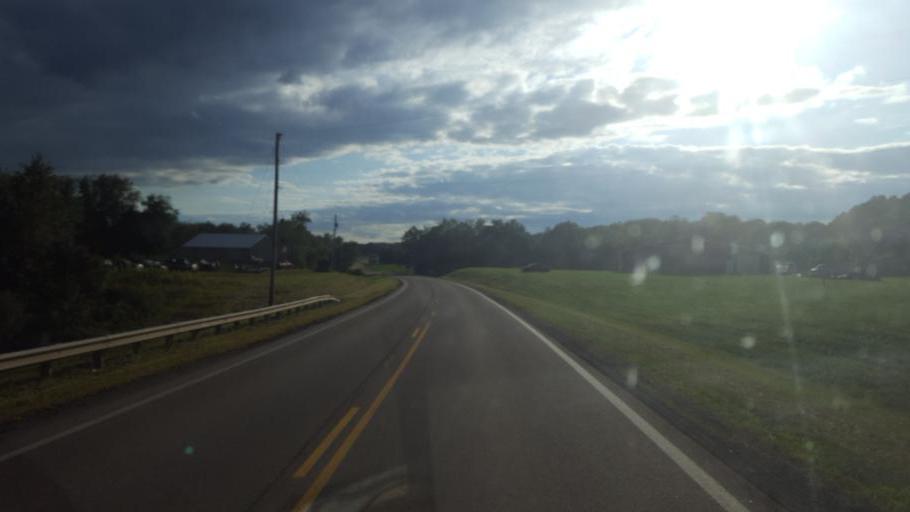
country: US
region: Ohio
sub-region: Knox County
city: Danville
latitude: 40.4612
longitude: -82.2151
